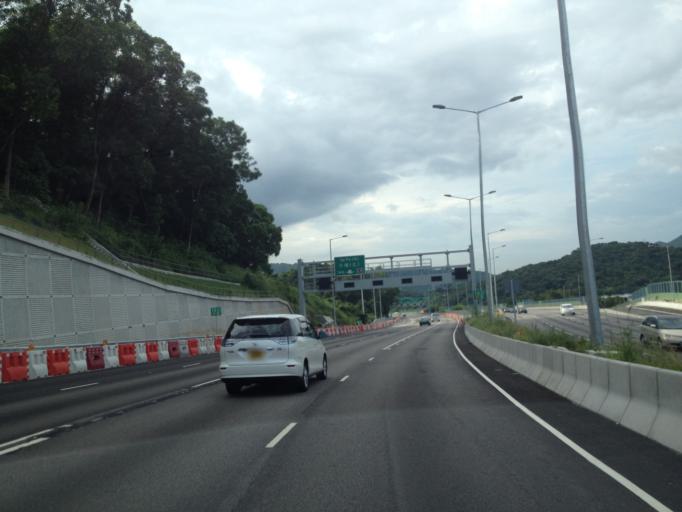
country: HK
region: Tai Po
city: Tai Po
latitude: 22.4475
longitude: 114.1545
